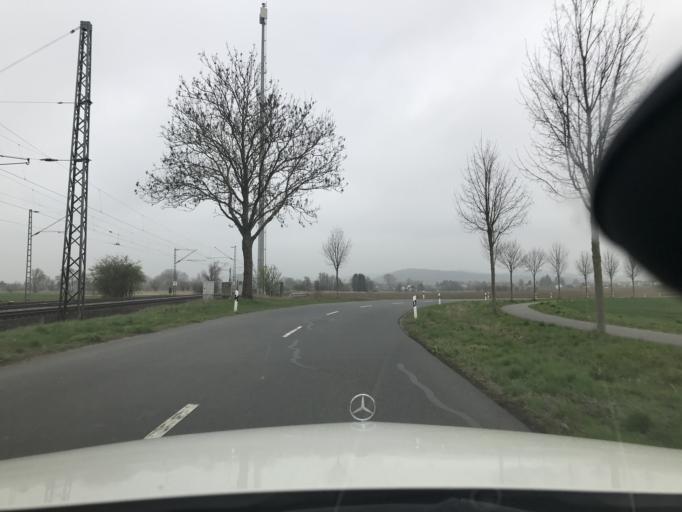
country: DE
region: Lower Saxony
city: Gemeinde Friedland
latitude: 51.4532
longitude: 9.9177
